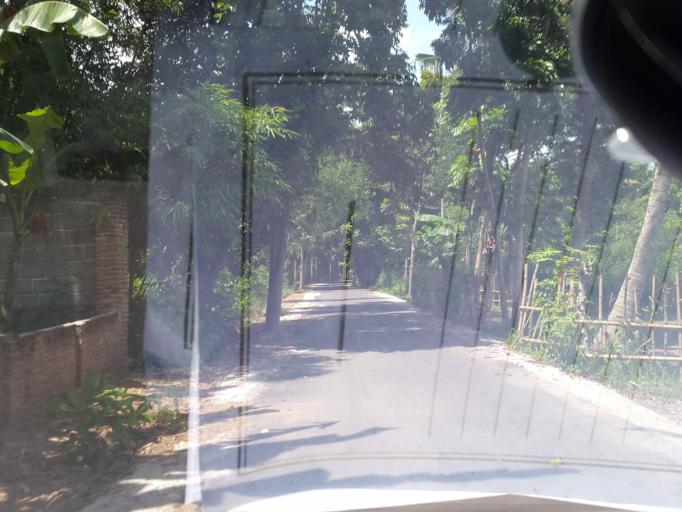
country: ID
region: West Nusa Tenggara
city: Jelateng Timur
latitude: -8.7126
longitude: 116.0738
